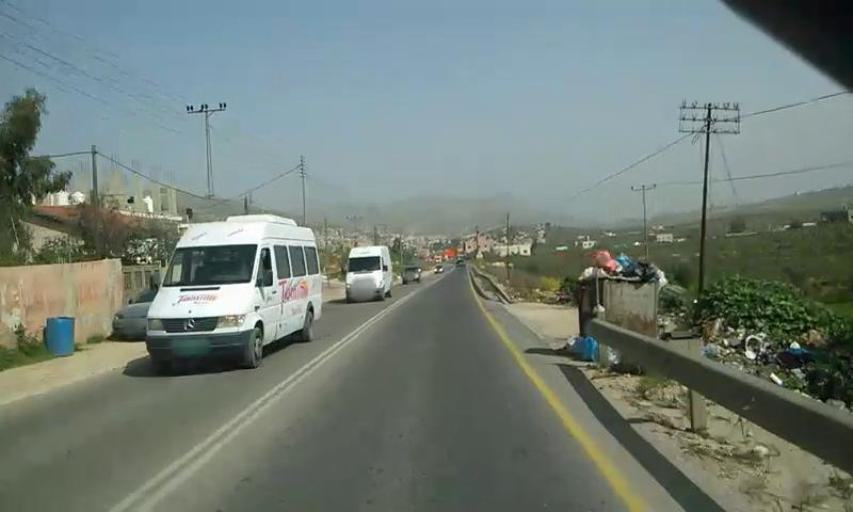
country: PS
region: West Bank
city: `Aynabus
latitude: 32.1333
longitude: 35.2578
